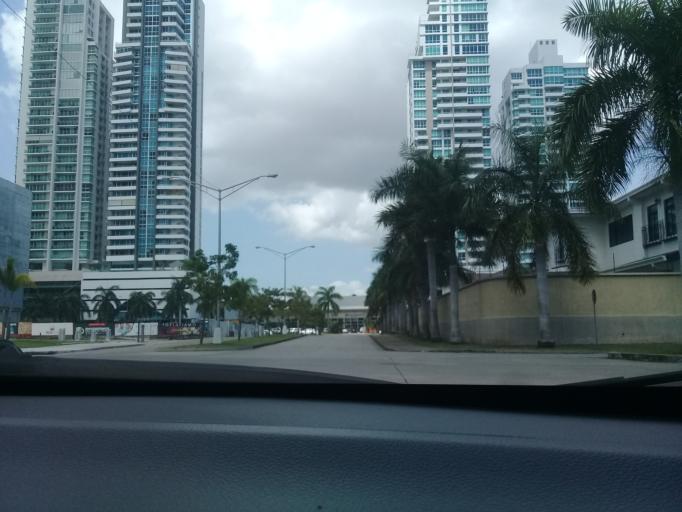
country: PA
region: Panama
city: San Miguelito
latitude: 9.0147
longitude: -79.4639
